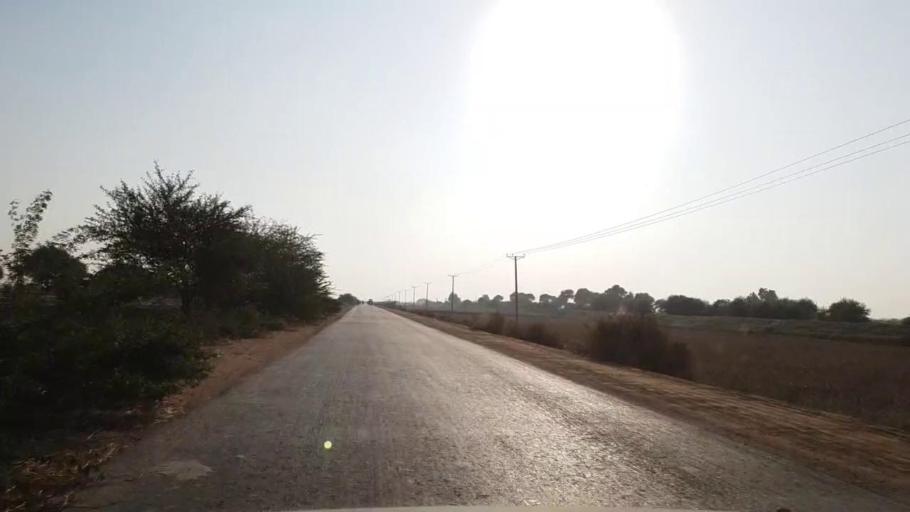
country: PK
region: Sindh
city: Mirpur Batoro
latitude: 24.7661
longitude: 68.2776
